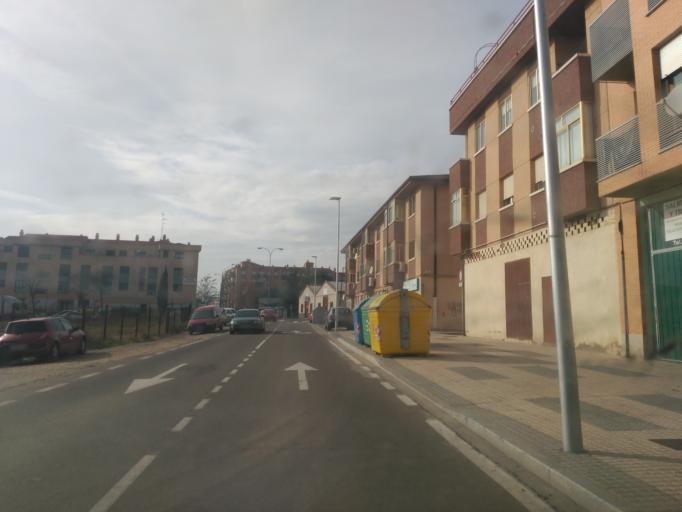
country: ES
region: Castille and Leon
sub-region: Provincia de Salamanca
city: Santa Marta de Tormes
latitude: 40.9724
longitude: -5.6381
